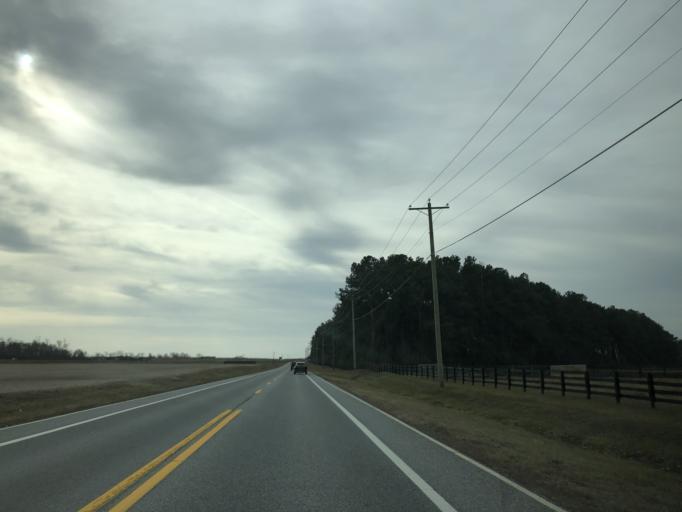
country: US
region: Delaware
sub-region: New Castle County
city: Middletown
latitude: 39.4711
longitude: -75.7386
